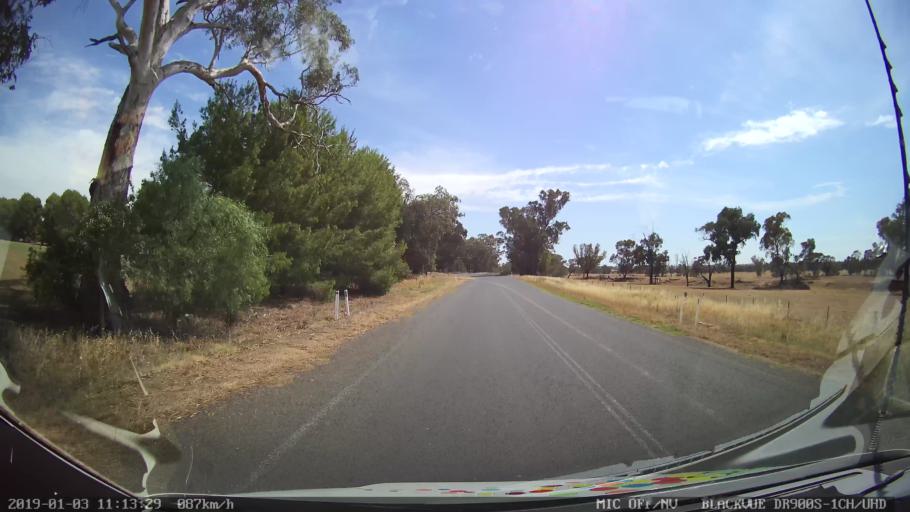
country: AU
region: New South Wales
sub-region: Young
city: Young
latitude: -34.1880
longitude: 148.2603
